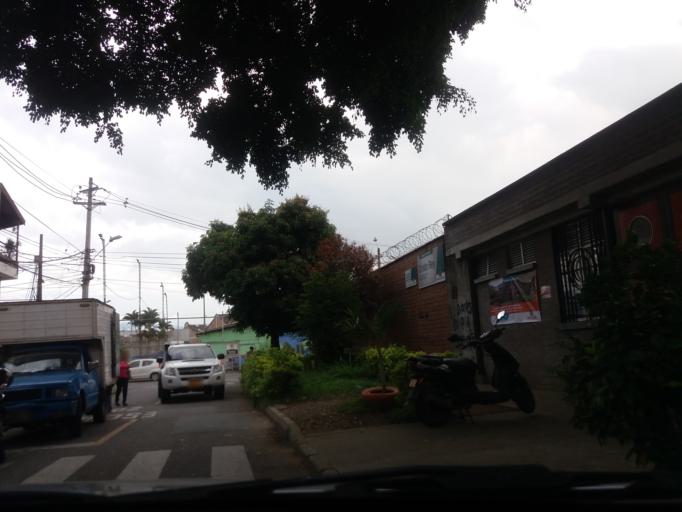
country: CO
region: Antioquia
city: Itagui
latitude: 6.2055
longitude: -75.5819
